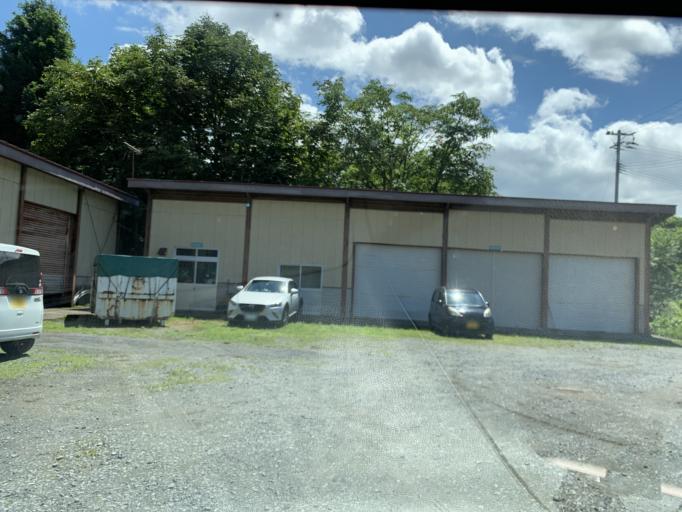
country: JP
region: Iwate
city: Ichinoseki
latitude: 38.9215
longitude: 141.0647
